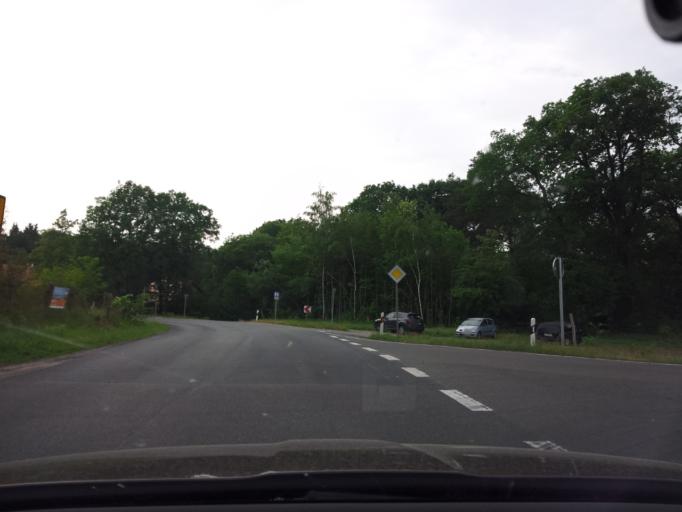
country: DE
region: Brandenburg
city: Michendorf
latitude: 52.3037
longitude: 12.9719
